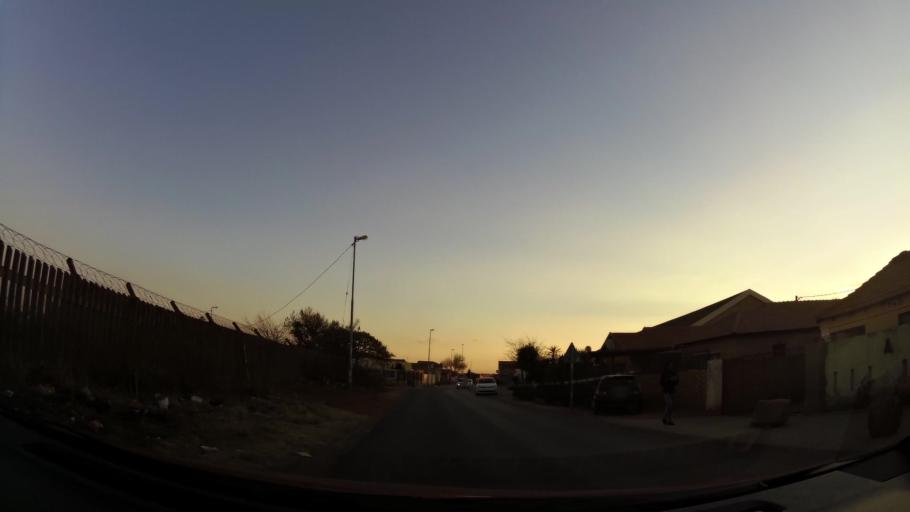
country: ZA
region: Gauteng
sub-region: City of Johannesburg Metropolitan Municipality
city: Soweto
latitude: -26.2270
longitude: 27.8436
